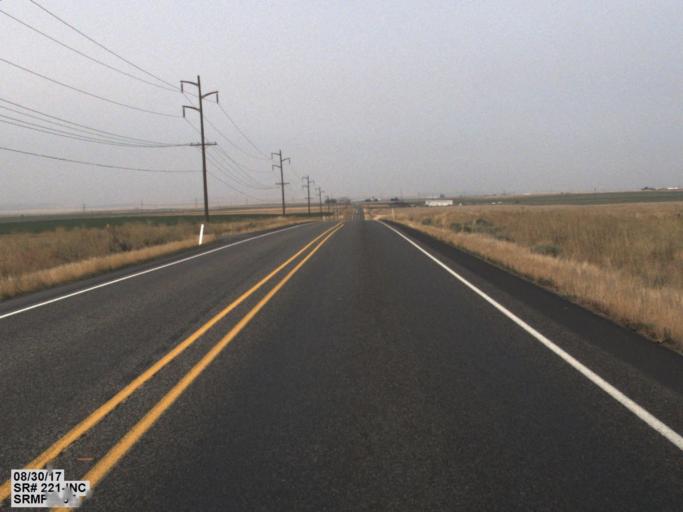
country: US
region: Oregon
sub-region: Morrow County
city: Irrigon
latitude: 46.0303
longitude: -119.6027
